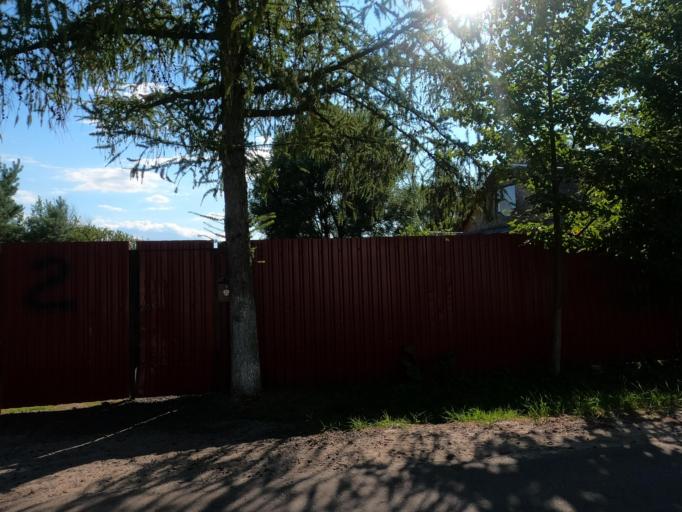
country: RU
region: Moskovskaya
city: Konobeyevo
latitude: 55.4073
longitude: 38.7028
